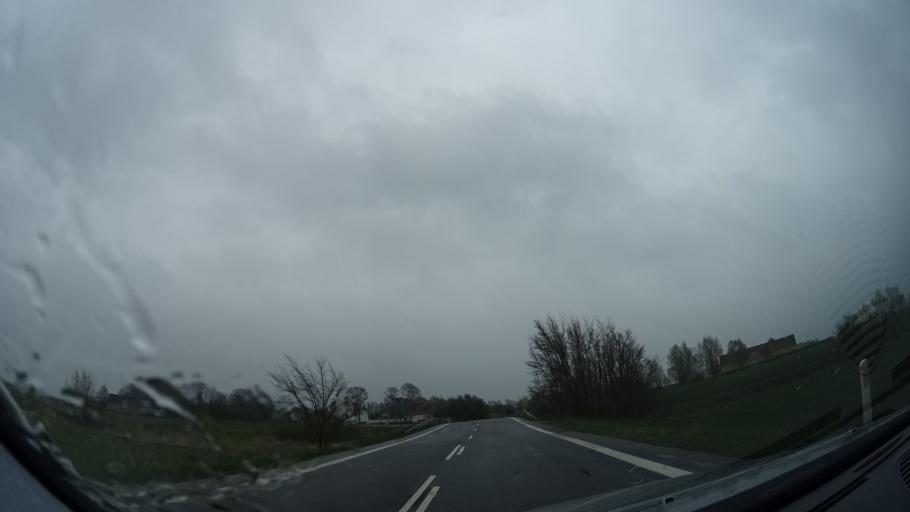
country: DK
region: Zealand
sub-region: Holbaek Kommune
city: Holbaek
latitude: 55.7168
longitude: 11.6127
